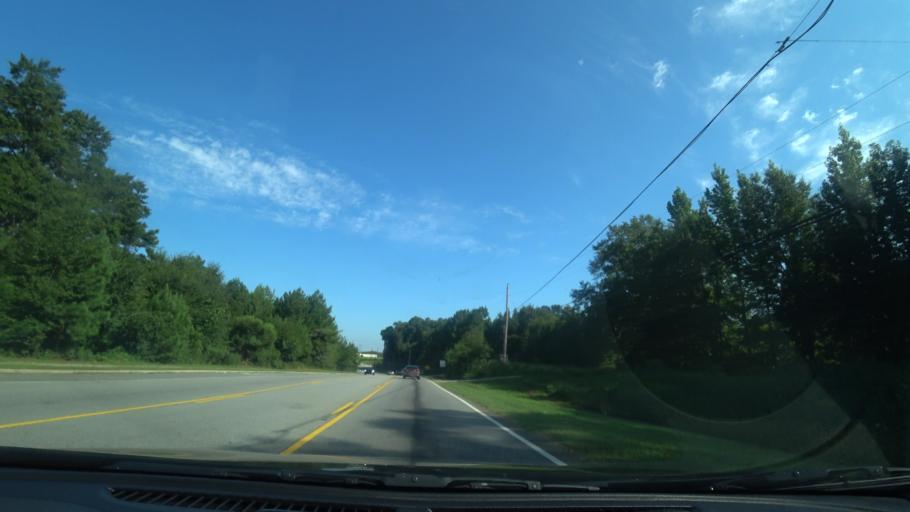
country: US
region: Georgia
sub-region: Gwinnett County
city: Lawrenceville
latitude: 33.9717
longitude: -83.9928
